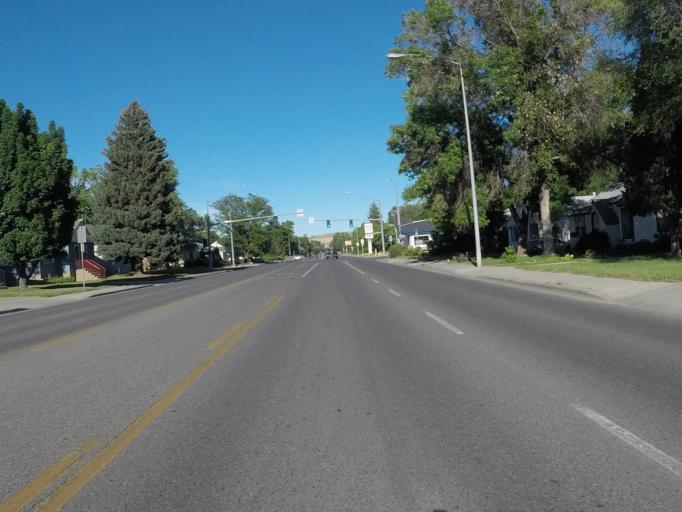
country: US
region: Montana
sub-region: Yellowstone County
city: Billings
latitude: 45.7771
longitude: -108.5370
